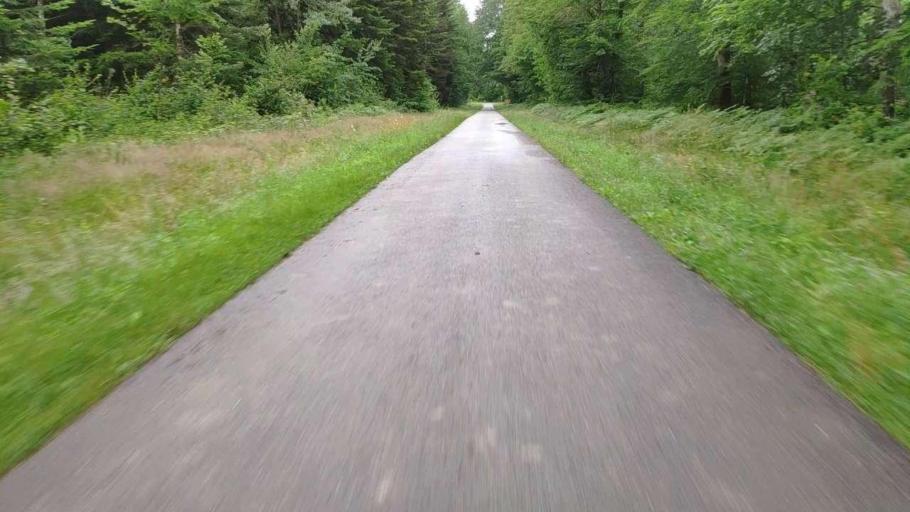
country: FR
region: Franche-Comte
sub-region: Departement du Jura
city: Chaussin
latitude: 46.8927
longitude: 5.4303
